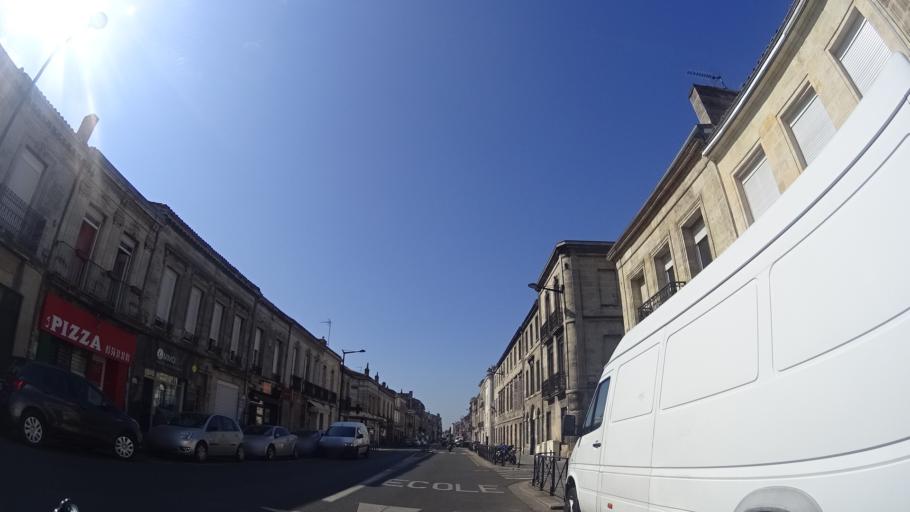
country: FR
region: Aquitaine
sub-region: Departement de la Gironde
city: Bordeaux
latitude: 44.8286
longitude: -0.5724
